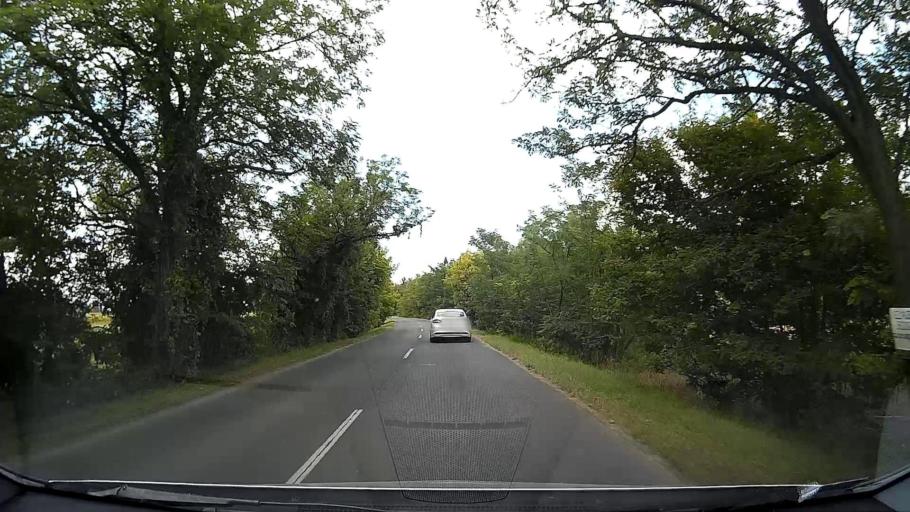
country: HU
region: Pest
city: Tahitotfalu
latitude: 47.7324
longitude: 19.1029
